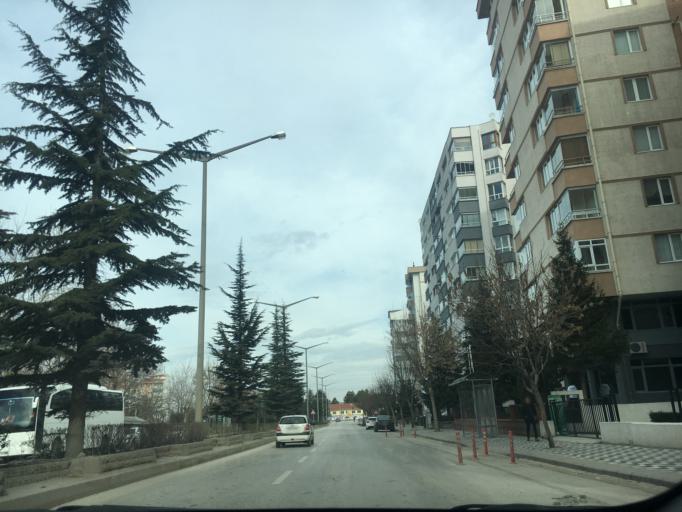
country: TR
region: Eskisehir
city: Eskisehir
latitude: 39.7716
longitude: 30.5014
